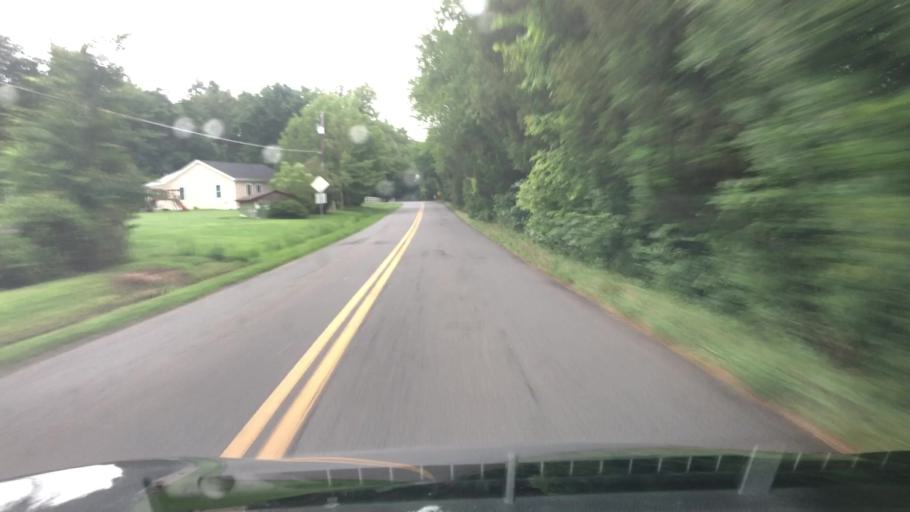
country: US
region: Virginia
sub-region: Prince William County
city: Nokesville
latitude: 38.6663
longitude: -77.6462
